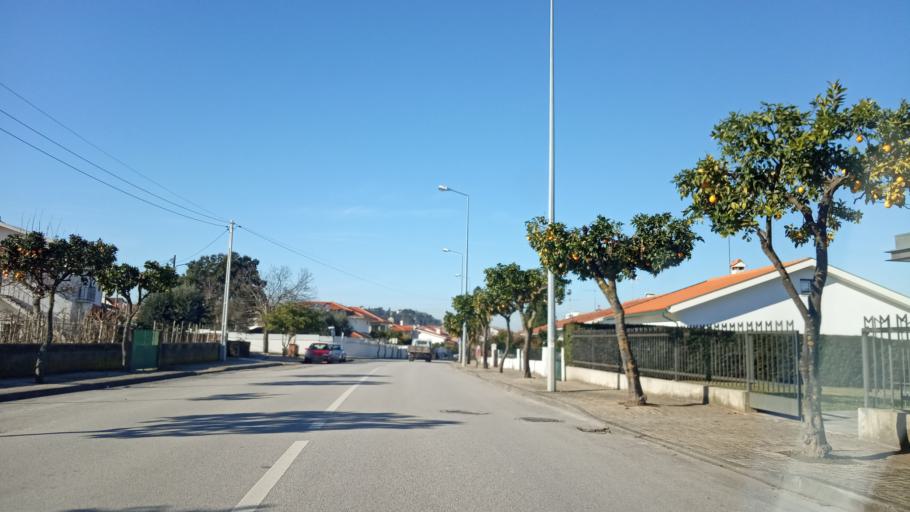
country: PT
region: Aveiro
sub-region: Anadia
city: Anadia
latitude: 40.4363
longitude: -8.4303
